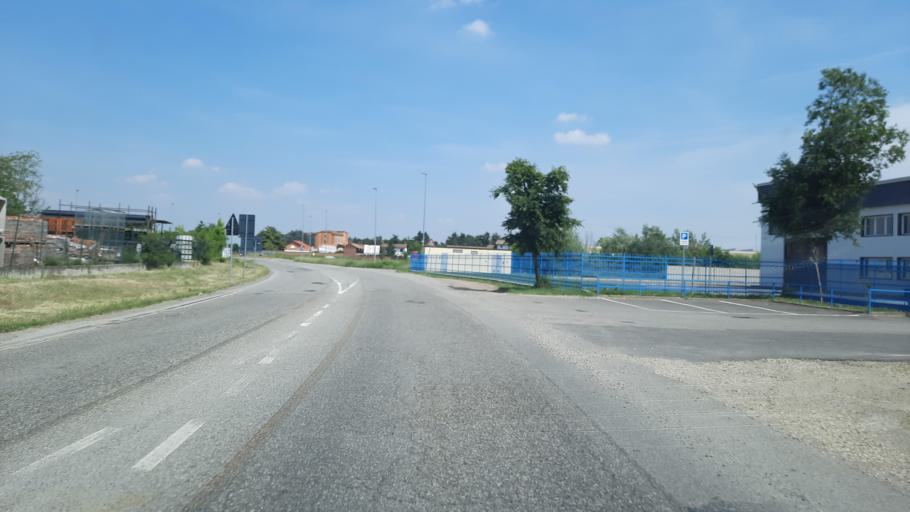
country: IT
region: Lombardy
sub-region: Provincia di Pavia
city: Garlasco
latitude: 45.1899
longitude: 8.9299
